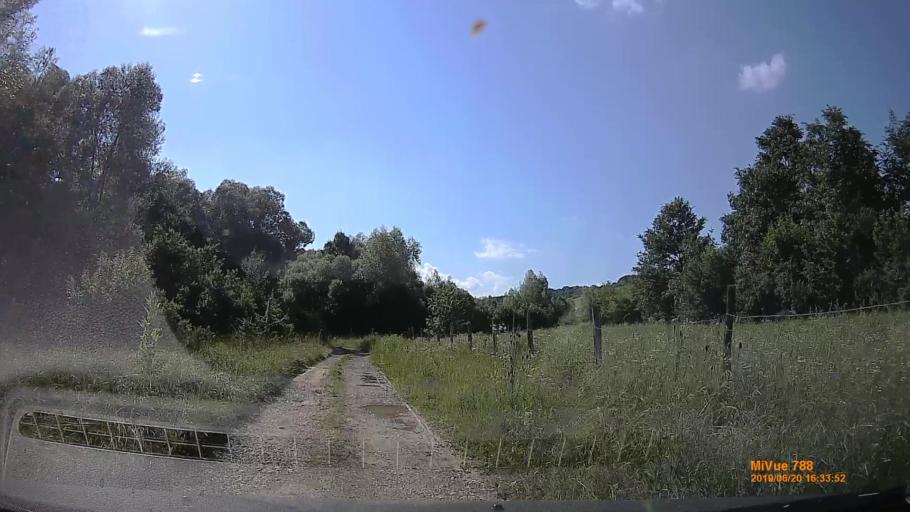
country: HU
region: Baranya
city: Buekkoesd
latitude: 46.1736
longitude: 18.0453
